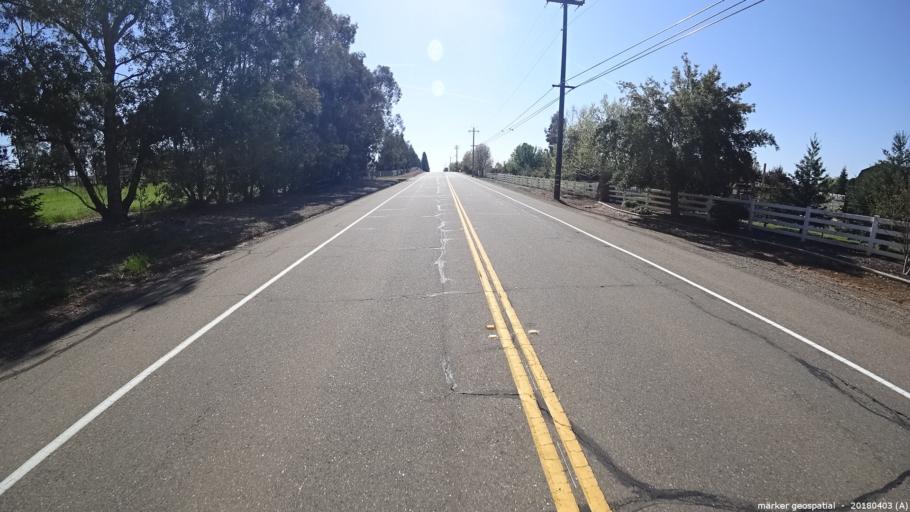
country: US
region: California
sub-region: Sacramento County
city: Clay
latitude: 38.4171
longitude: -121.1818
